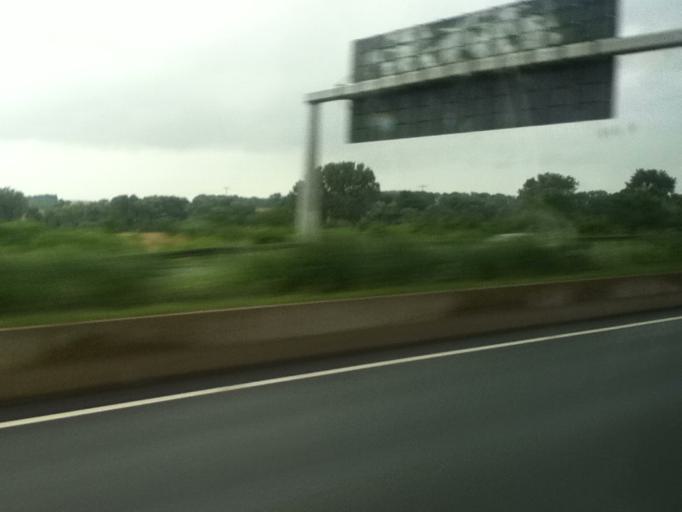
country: DE
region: Thuringia
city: Horselgau
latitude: 50.9068
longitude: 10.6237
